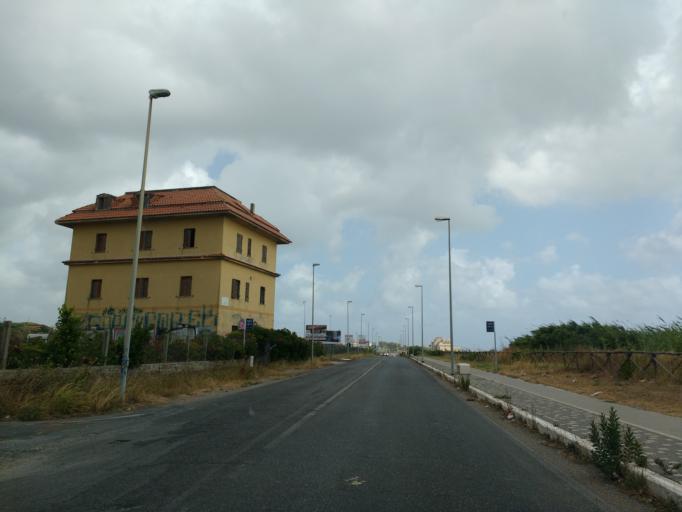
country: IT
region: Latium
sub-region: Citta metropolitana di Roma Capitale
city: Anzio
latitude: 41.4736
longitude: 12.6045
